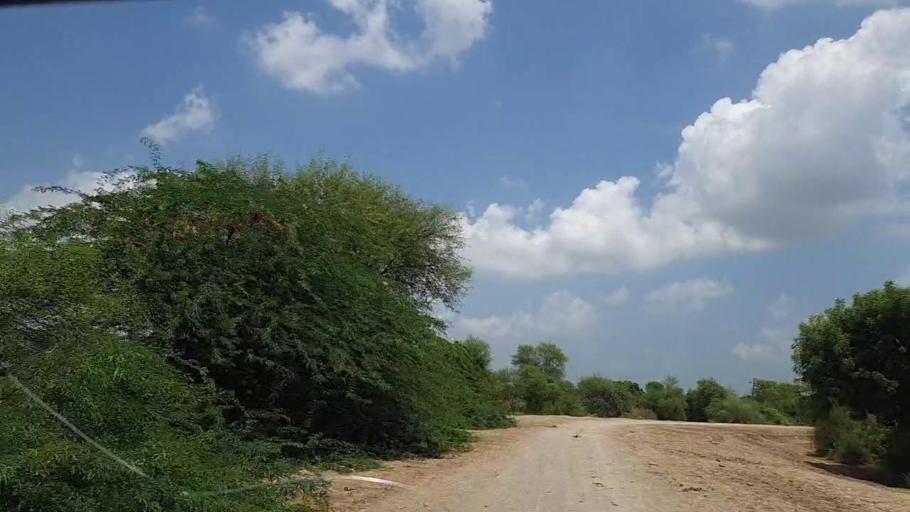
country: PK
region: Sindh
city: Tharu Shah
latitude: 26.9512
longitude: 68.0217
